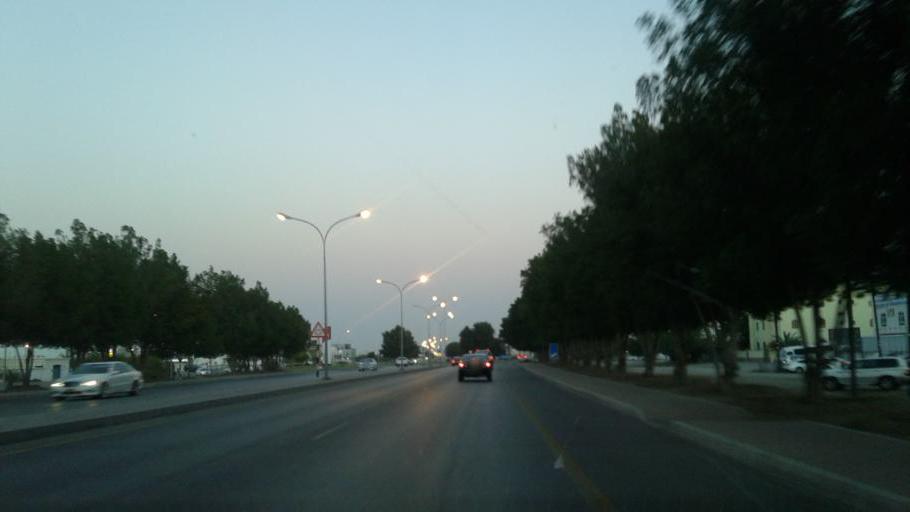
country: OM
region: Muhafazat Masqat
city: As Sib al Jadidah
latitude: 23.6145
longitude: 58.2173
